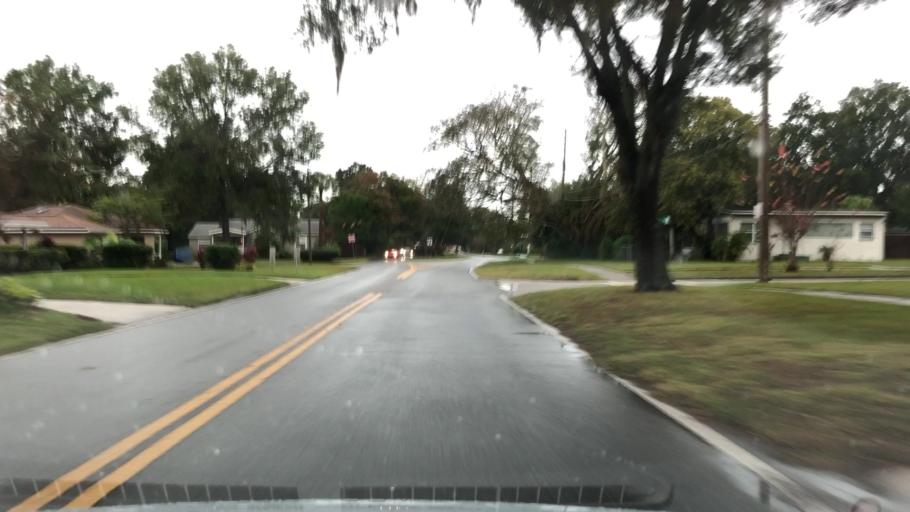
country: US
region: Florida
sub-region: Orange County
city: Orlando
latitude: 28.5344
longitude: -81.3476
